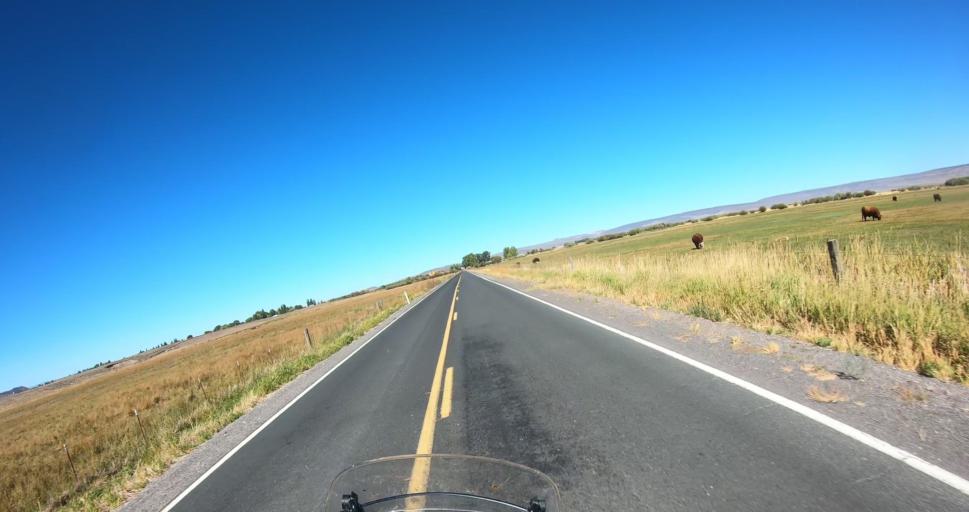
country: US
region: Oregon
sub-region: Lake County
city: Lakeview
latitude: 42.6766
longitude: -120.5283
